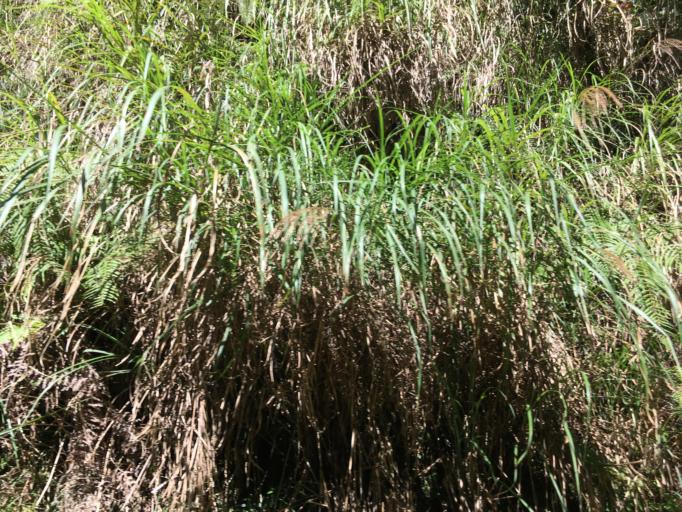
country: TW
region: Taiwan
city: Daxi
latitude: 24.5539
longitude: 121.3969
